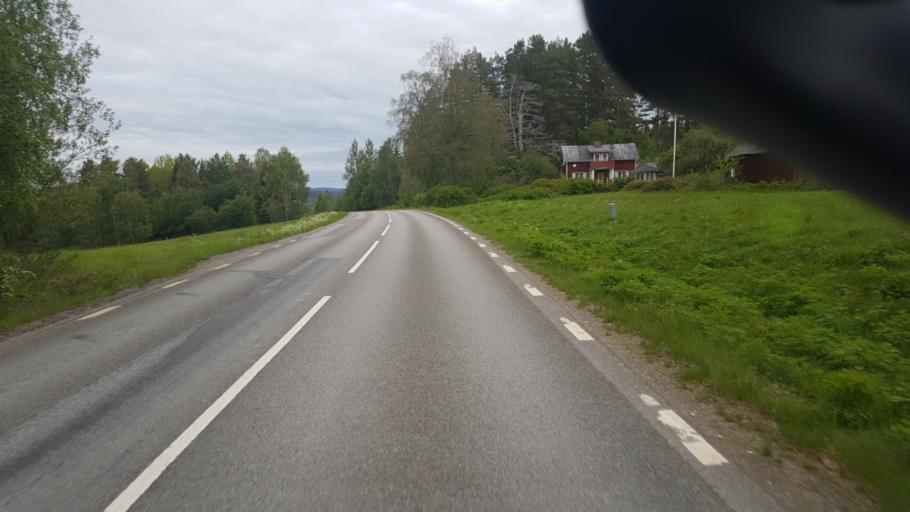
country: SE
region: Vaermland
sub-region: Arvika Kommun
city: Arvika
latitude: 59.7363
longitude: 12.5608
